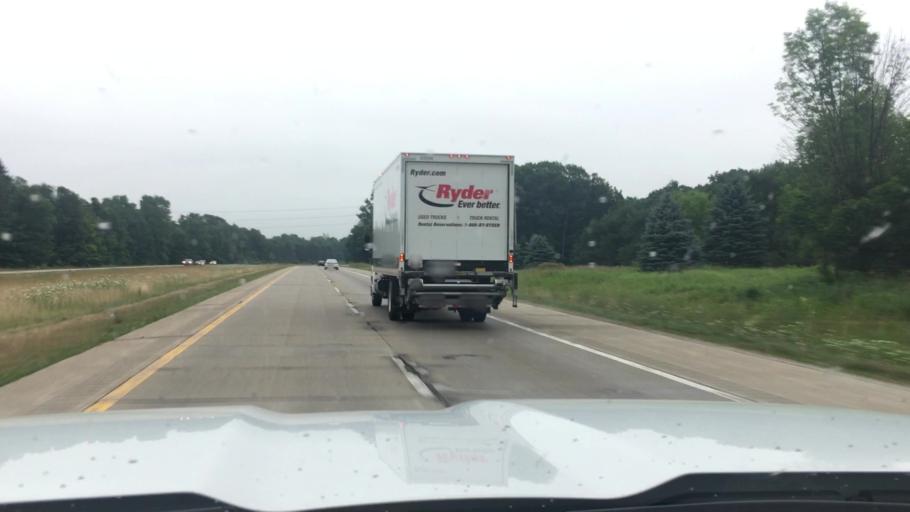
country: US
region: Michigan
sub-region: Eaton County
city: Waverly
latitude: 42.8038
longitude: -84.6322
